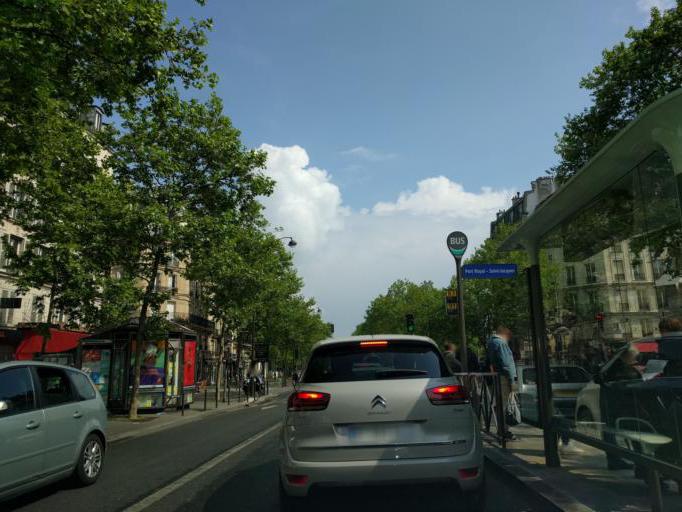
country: FR
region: Ile-de-France
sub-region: Paris
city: Paris
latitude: 48.8390
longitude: 2.3391
